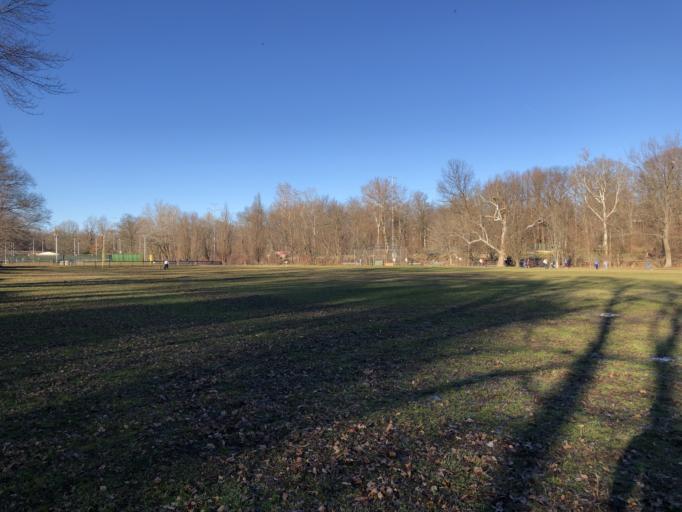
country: US
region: Virginia
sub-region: Fairfax County
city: Baileys Crossroads
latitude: 38.8708
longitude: -77.1332
